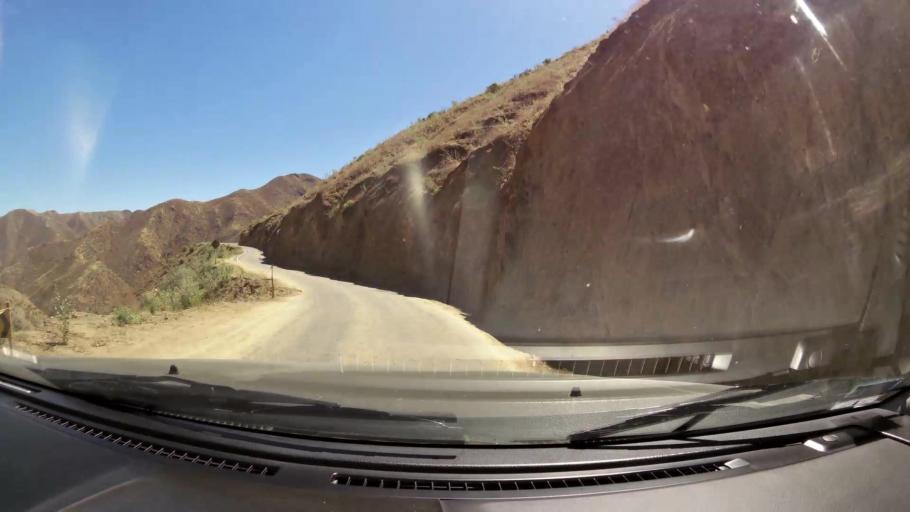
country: PE
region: Ica
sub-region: Provincia de Pisco
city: Huancano
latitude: -13.7241
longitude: -75.4568
